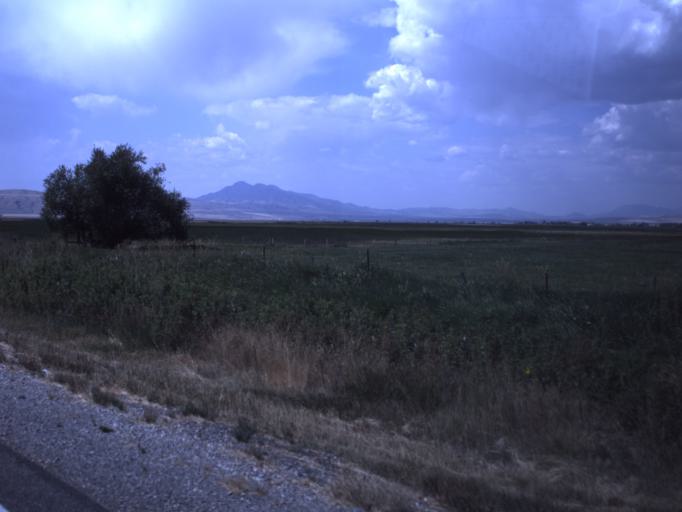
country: US
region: Utah
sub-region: Cache County
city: Benson
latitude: 41.7425
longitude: -111.9150
